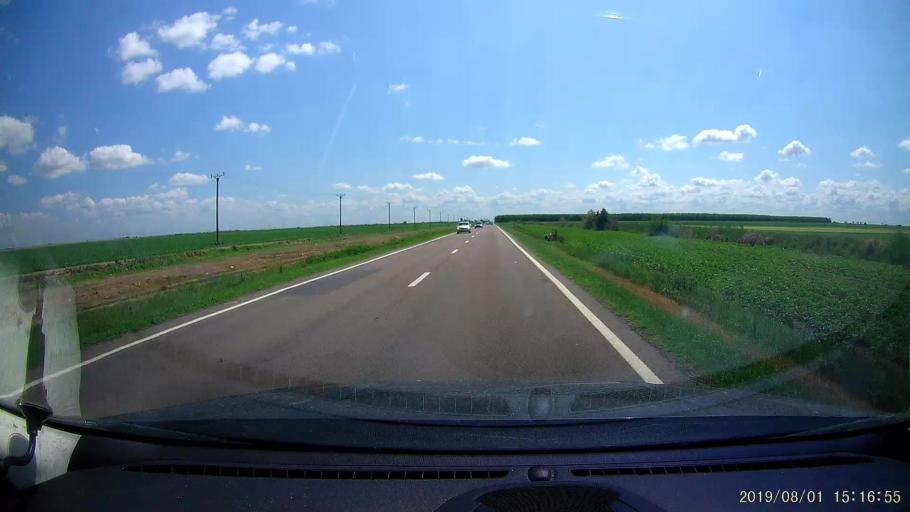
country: RO
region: Braila
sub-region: Comuna Unirea
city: Unirea
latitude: 45.1380
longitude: 27.8447
